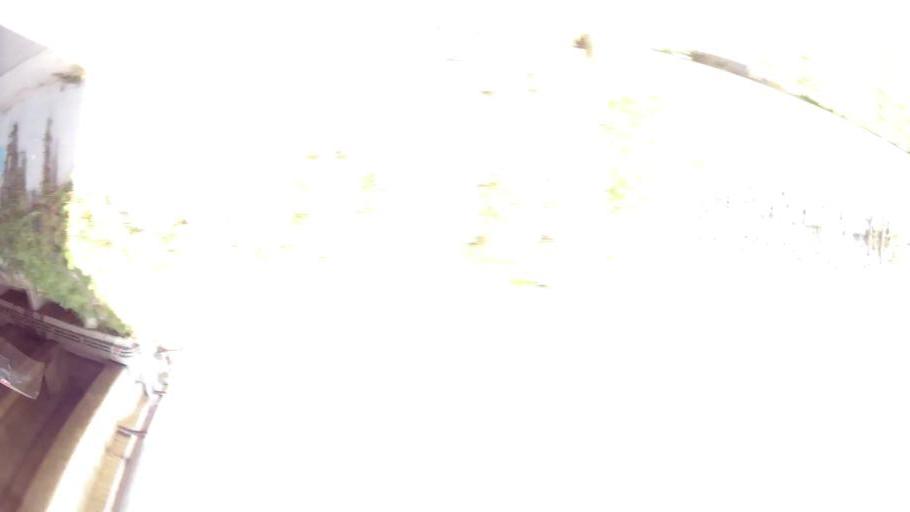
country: CL
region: Santiago Metropolitan
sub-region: Provincia de Santiago
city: Lo Prado
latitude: -33.4249
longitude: -70.7831
